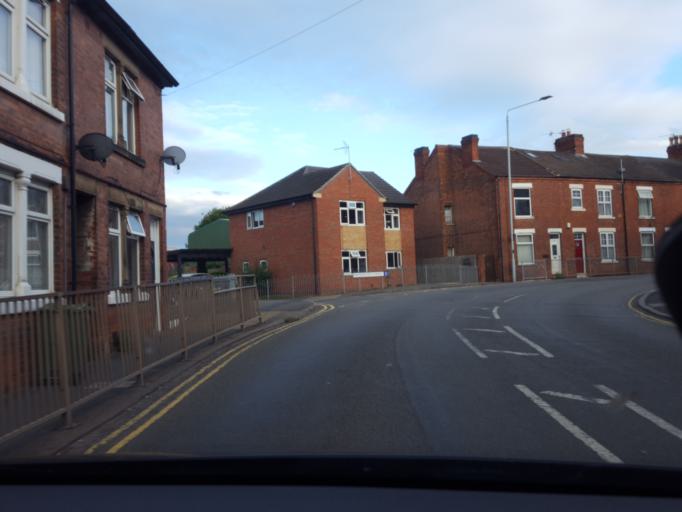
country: GB
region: England
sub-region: Leicestershire
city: Loughborough
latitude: 52.7743
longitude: -1.1969
